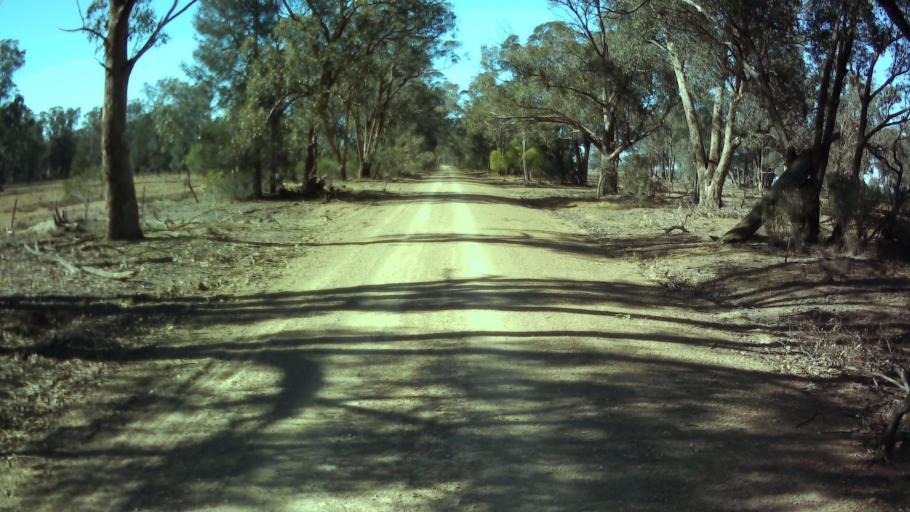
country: AU
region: New South Wales
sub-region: Weddin
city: Grenfell
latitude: -33.9382
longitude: 147.8715
